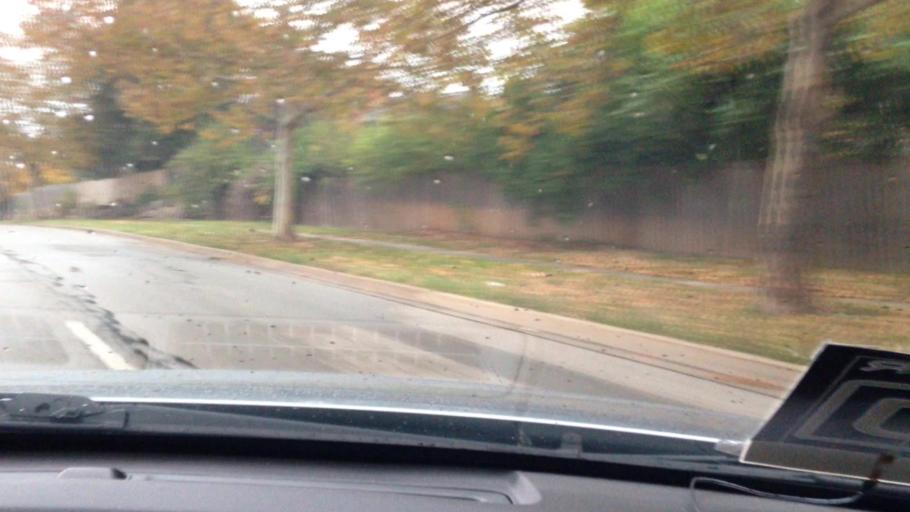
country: US
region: Missouri
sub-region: Platte County
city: Riverside
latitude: 39.2105
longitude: -94.6329
